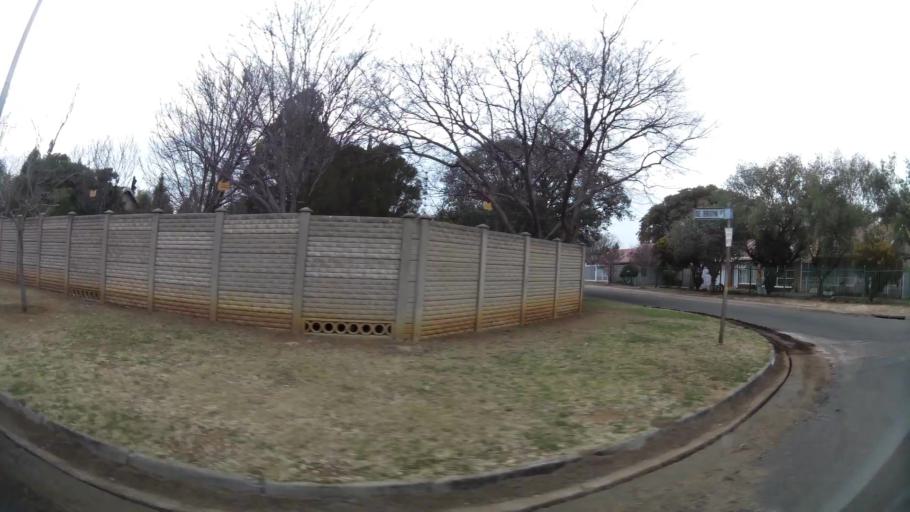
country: ZA
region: Orange Free State
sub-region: Mangaung Metropolitan Municipality
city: Bloemfontein
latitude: -29.1160
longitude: 26.1654
